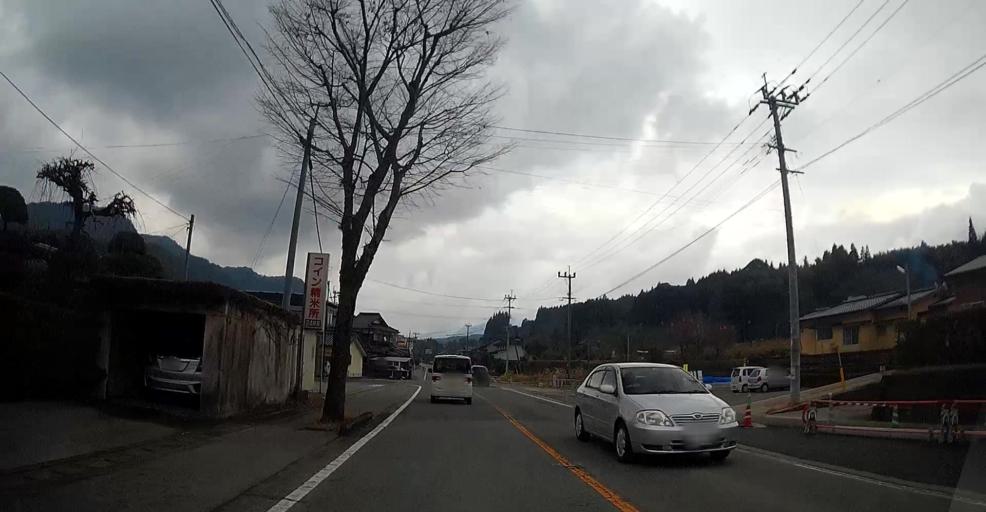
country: JP
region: Kumamoto
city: Matsubase
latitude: 32.6223
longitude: 130.8218
